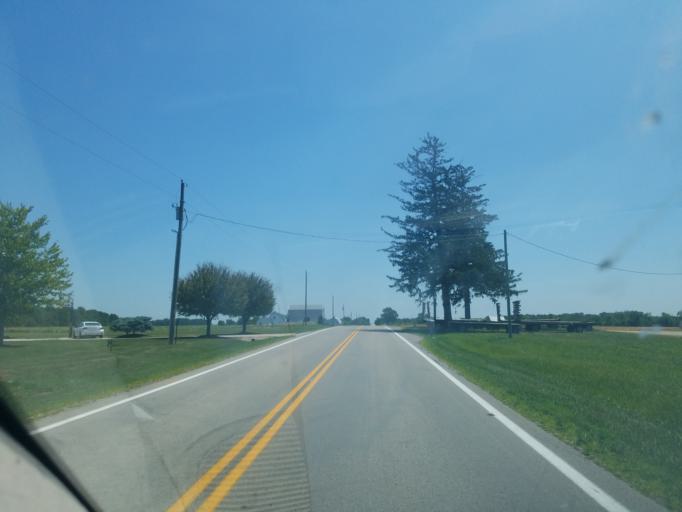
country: US
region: Ohio
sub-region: Mercer County
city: Rockford
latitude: 40.7424
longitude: -84.7179
